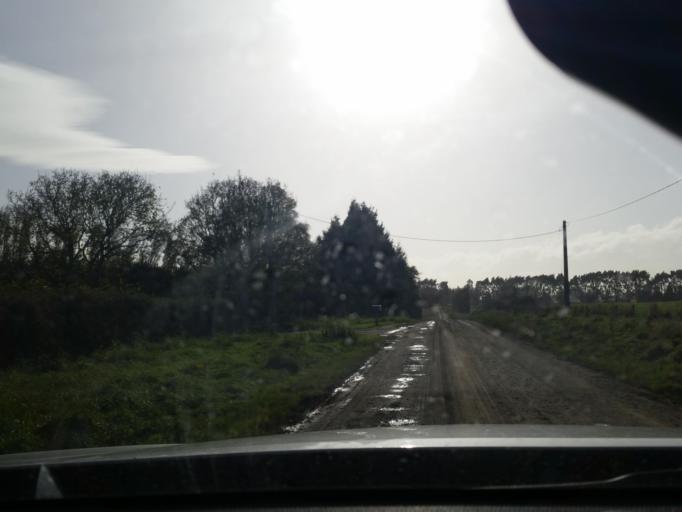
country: NZ
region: Southland
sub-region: Invercargill City
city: Invercargill
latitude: -46.2783
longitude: 168.2934
